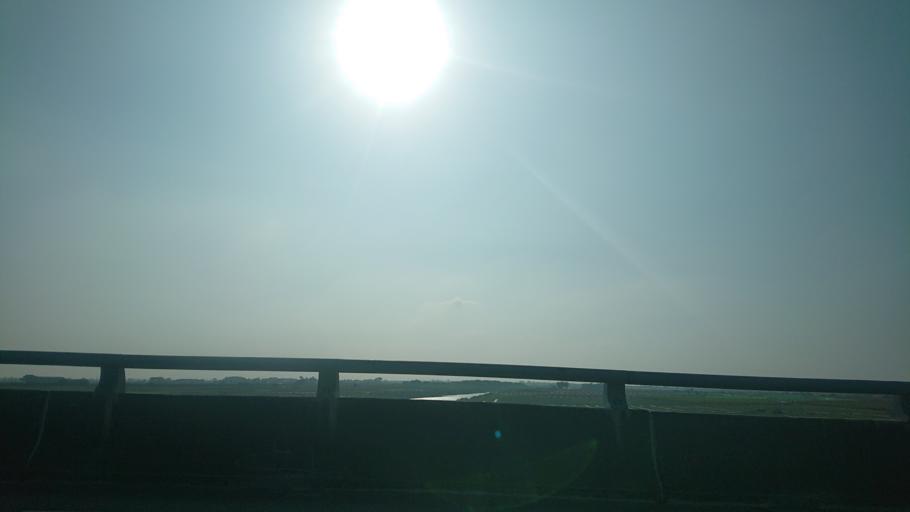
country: TW
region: Taiwan
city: Xinying
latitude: 23.3293
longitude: 120.2523
